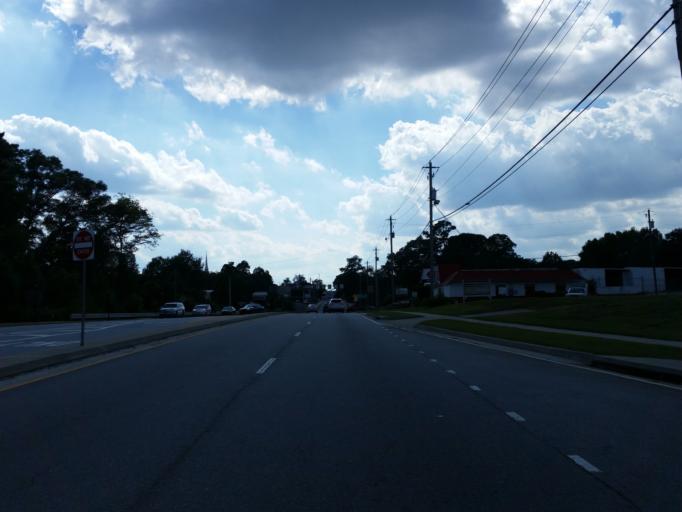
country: US
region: Georgia
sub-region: Gwinnett County
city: Lawrenceville
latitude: 33.9568
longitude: -83.9798
